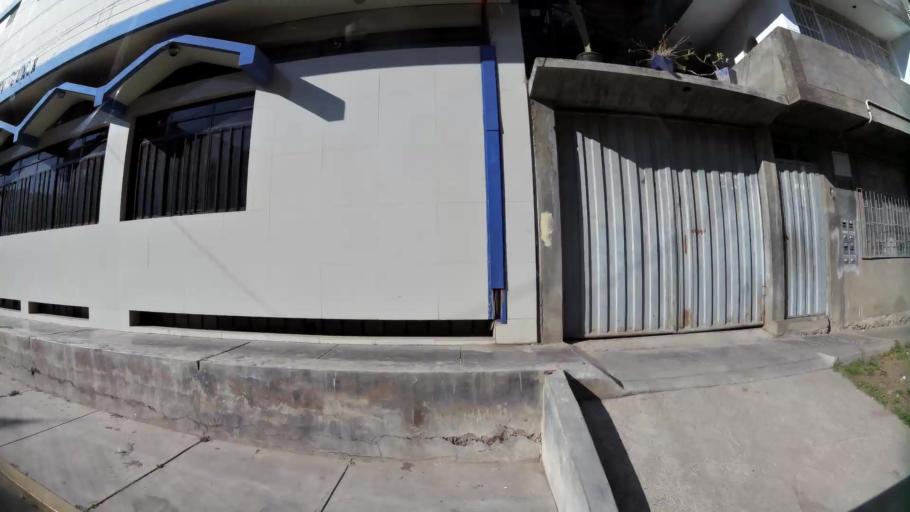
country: PE
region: Junin
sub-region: Provincia de Huancayo
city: El Tambo
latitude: -12.0605
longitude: -75.2253
